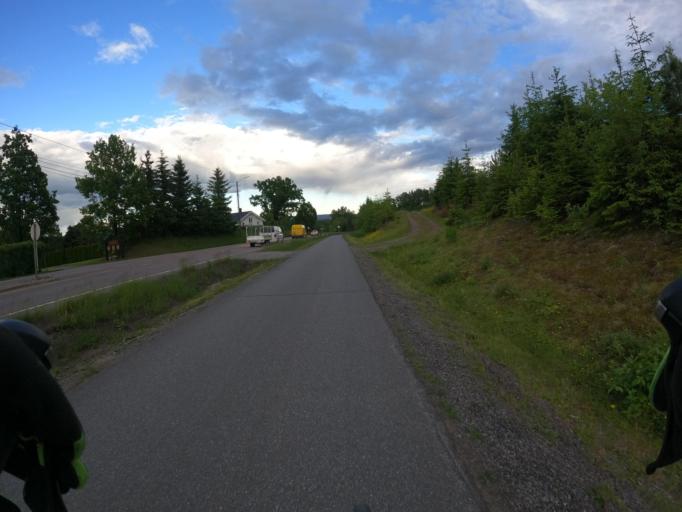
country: NO
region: Akershus
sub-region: Lorenskog
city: Kjenn
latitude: 59.9832
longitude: 10.9626
